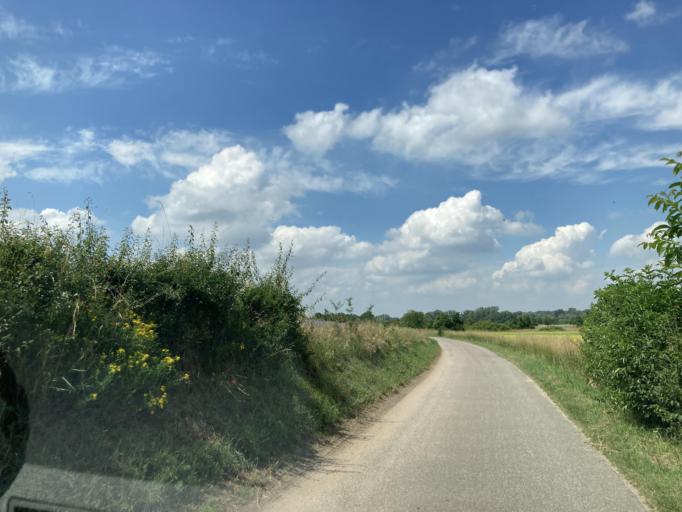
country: DE
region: Baden-Wuerttemberg
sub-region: Karlsruhe Region
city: Oberhausen-Rheinhausen
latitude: 49.2663
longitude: 8.4909
